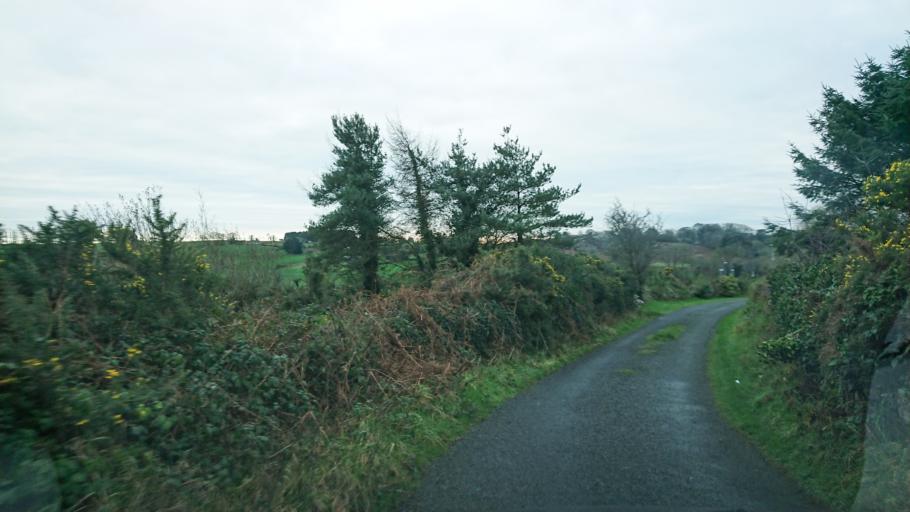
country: IE
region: Leinster
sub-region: Kilkenny
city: Mooncoin
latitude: 52.2145
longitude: -7.2712
